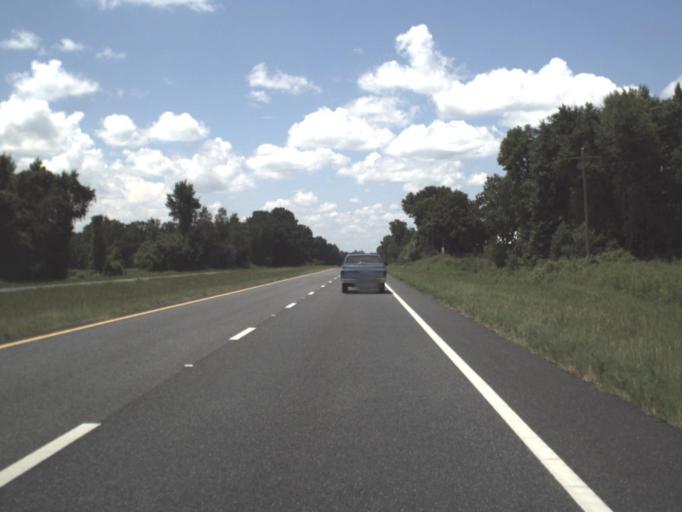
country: US
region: Florida
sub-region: Jefferson County
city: Monticello
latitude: 30.3279
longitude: -83.7715
